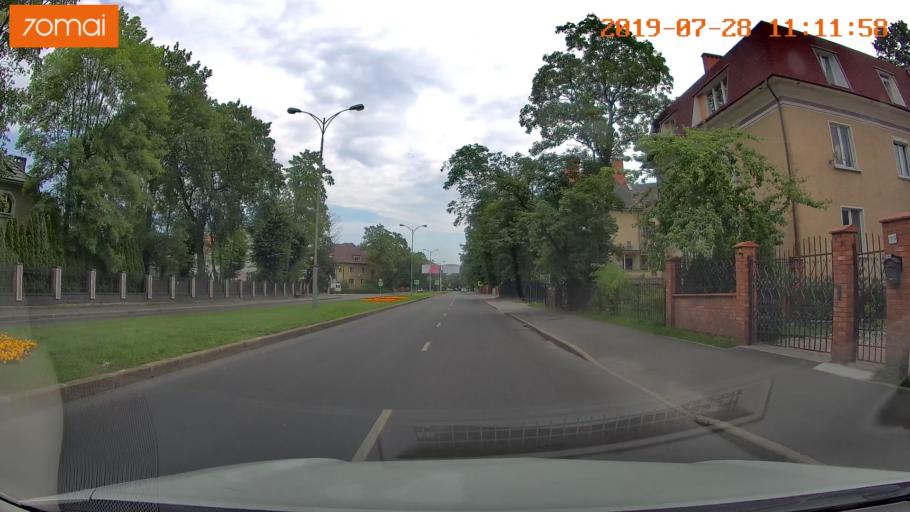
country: RU
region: Kaliningrad
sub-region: Gorod Kaliningrad
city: Kaliningrad
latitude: 54.7171
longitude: 20.4641
